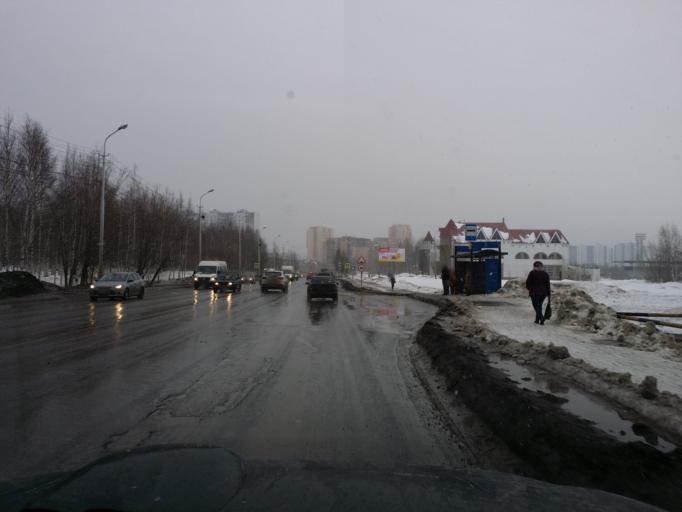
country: RU
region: Khanty-Mansiyskiy Avtonomnyy Okrug
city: Nizhnevartovsk
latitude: 60.9309
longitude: 76.5608
